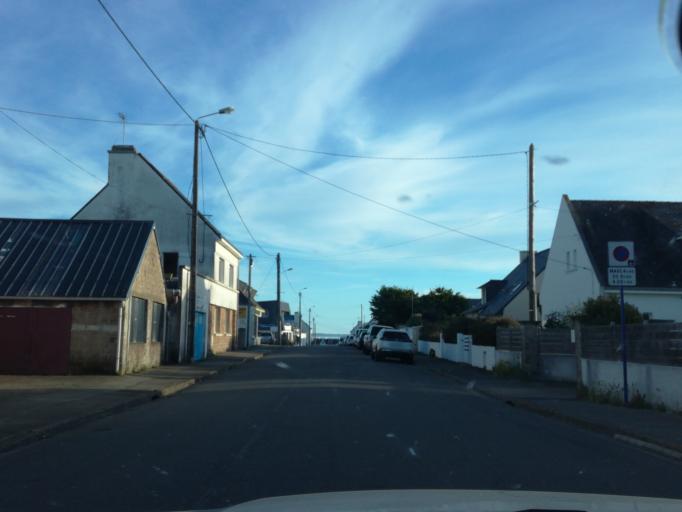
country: FR
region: Brittany
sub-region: Departement du Morbihan
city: Quiberon
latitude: 47.4776
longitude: -3.1288
